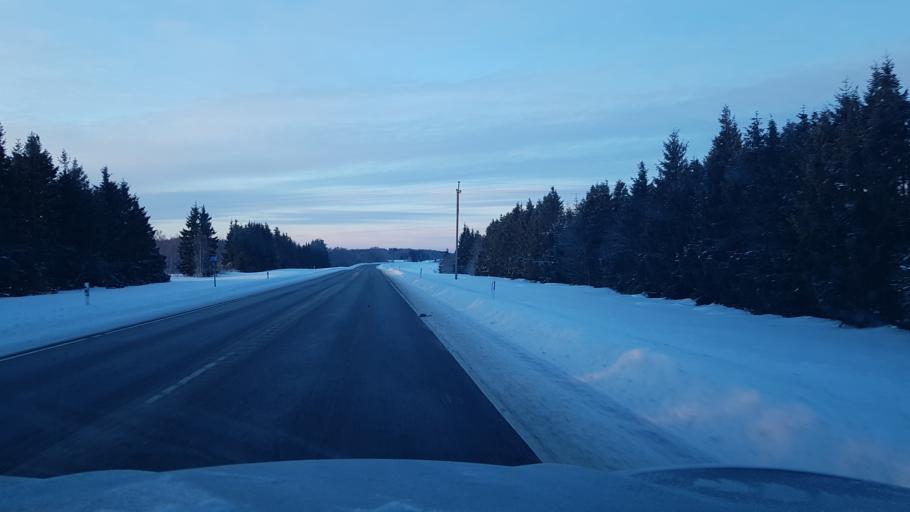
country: EE
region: Ida-Virumaa
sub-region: Narva-Joesuu linn
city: Narva-Joesuu
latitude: 59.3881
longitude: 27.9763
